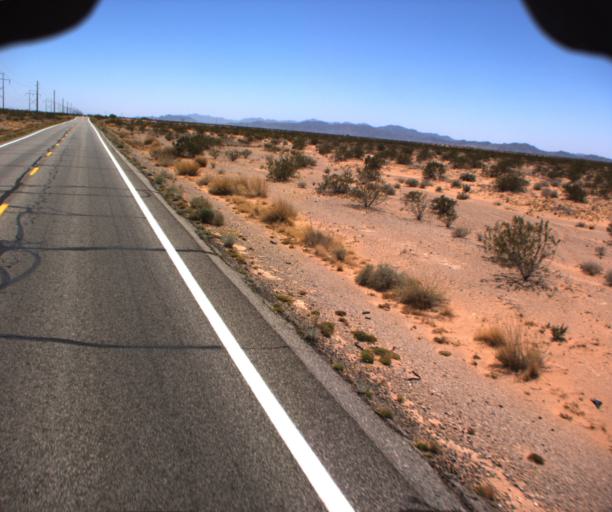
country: US
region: Arizona
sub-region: La Paz County
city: Quartzsite
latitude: 33.8670
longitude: -114.2170
